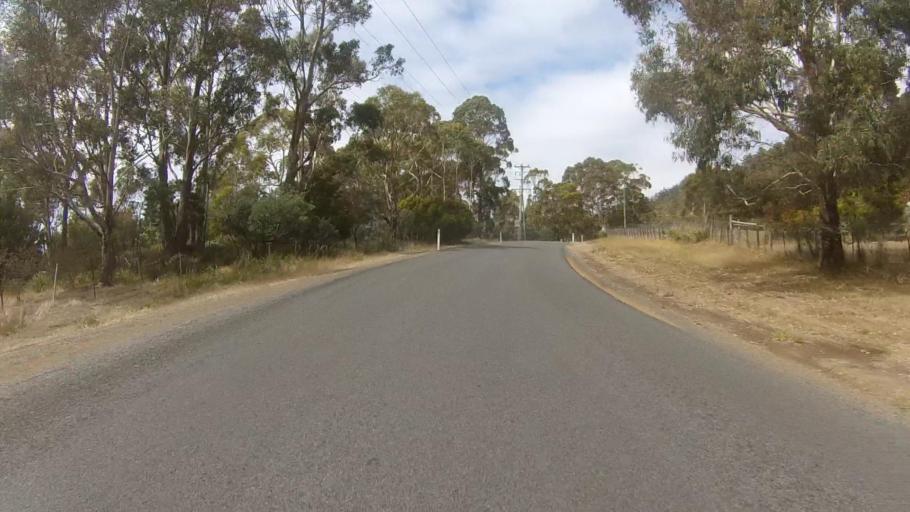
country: AU
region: Tasmania
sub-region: Kingborough
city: Blackmans Bay
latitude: -43.0227
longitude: 147.3229
